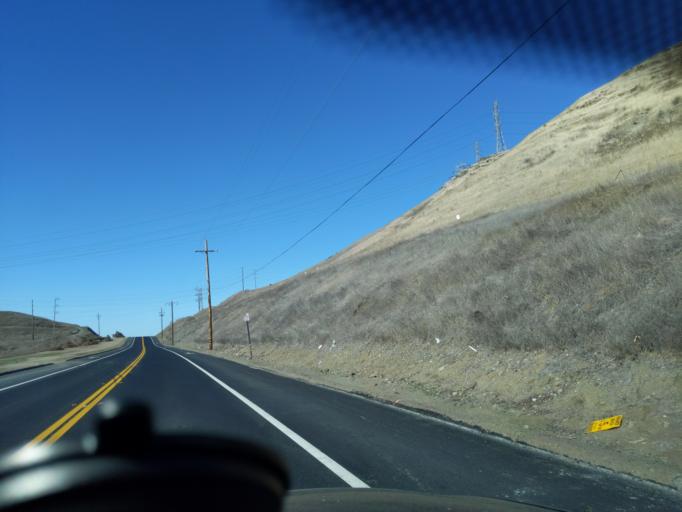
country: US
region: California
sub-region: Santa Clara County
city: Seven Trees
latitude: 37.2156
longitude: -121.7541
